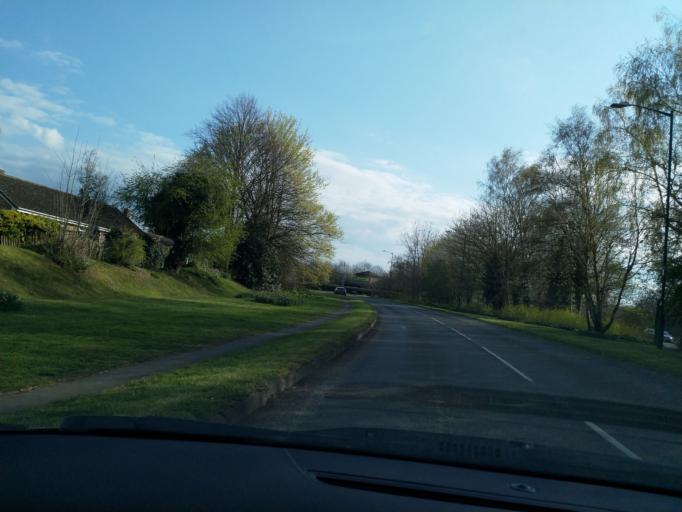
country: GB
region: England
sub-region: Warwickshire
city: Wellesbourne Mountford
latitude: 52.1924
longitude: -1.5975
